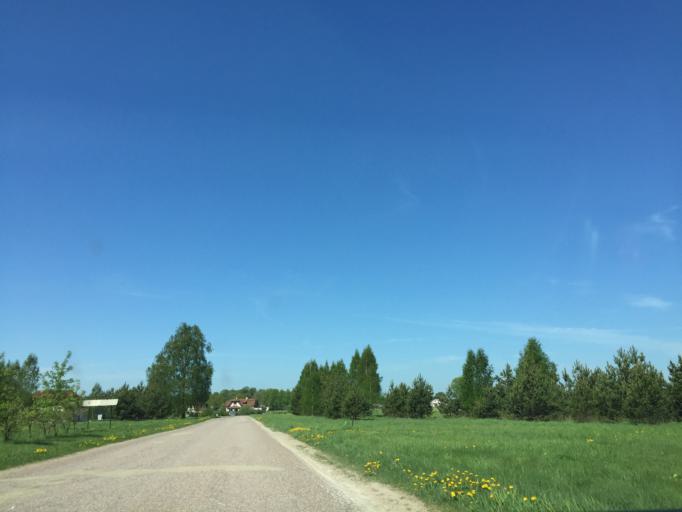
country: LV
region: Ogre
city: Ogre
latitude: 56.8536
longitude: 24.7069
